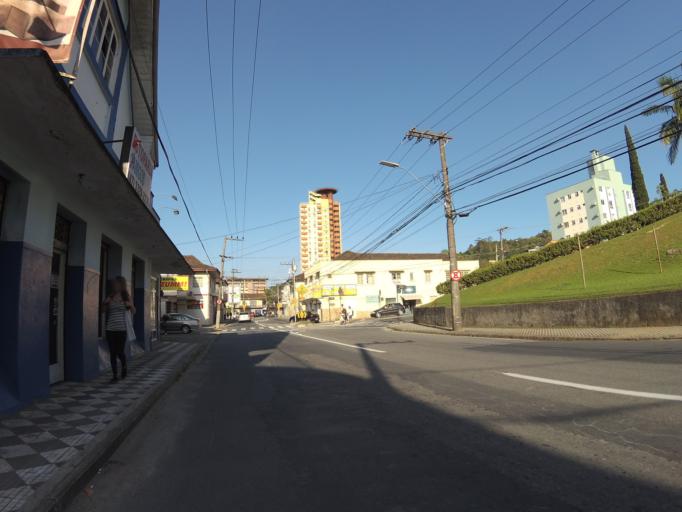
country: BR
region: Santa Catarina
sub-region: Blumenau
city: Blumenau
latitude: -26.9184
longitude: -49.0887
